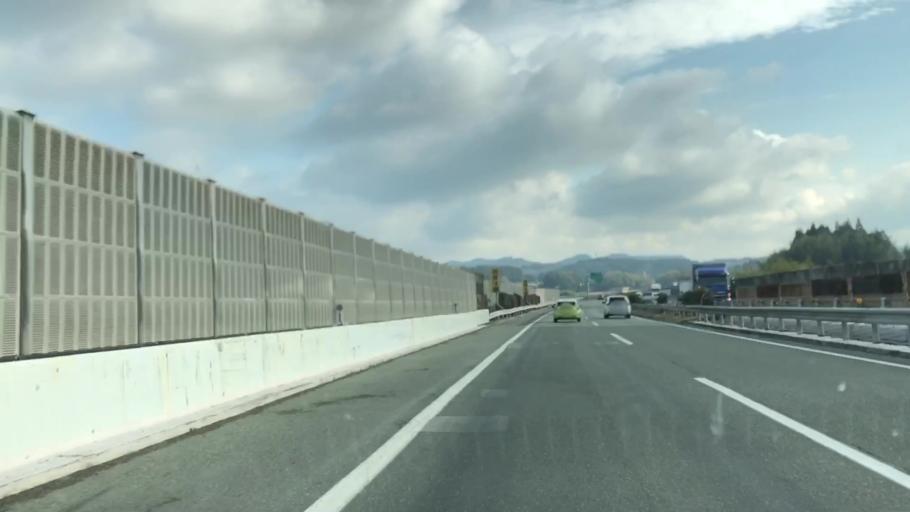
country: JP
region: Kumamoto
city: Tamana
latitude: 32.9966
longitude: 130.5961
